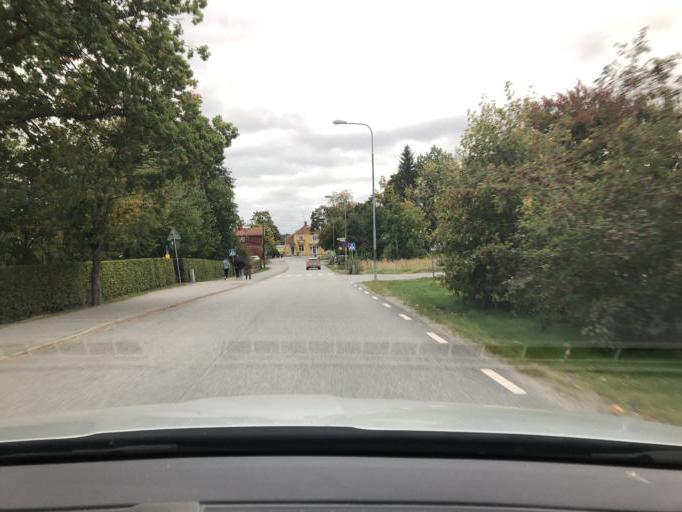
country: SE
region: Stockholm
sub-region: Haninge Kommun
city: Jordbro
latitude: 59.1042
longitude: 18.0434
